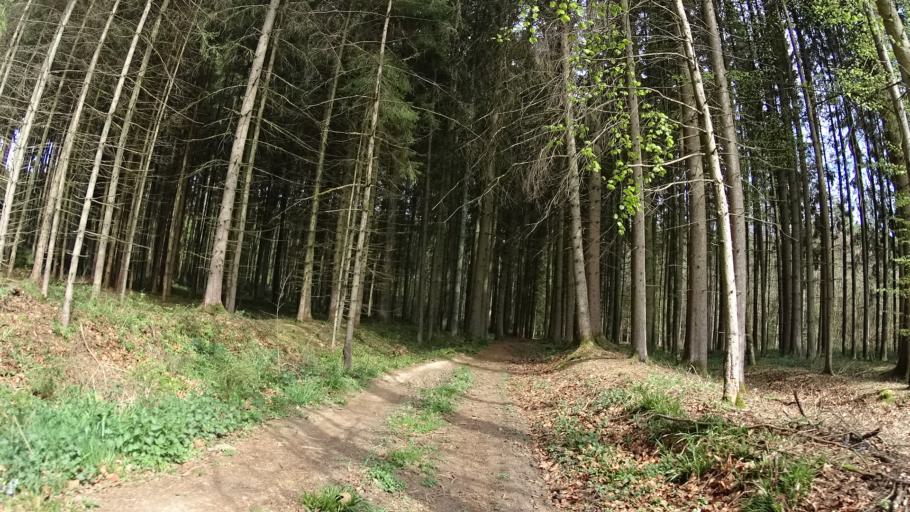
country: DE
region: Bavaria
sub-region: Upper Bavaria
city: Bohmfeld
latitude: 48.8613
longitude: 11.4034
